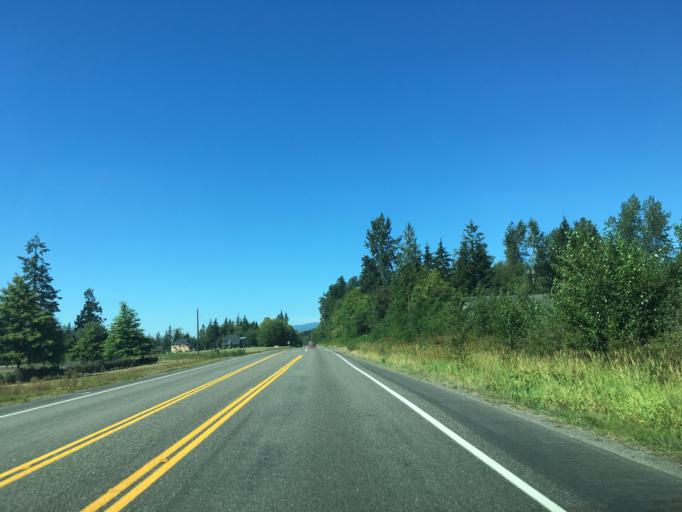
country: US
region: Washington
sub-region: Snohomish County
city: Sisco Heights
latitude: 48.1393
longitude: -122.1129
